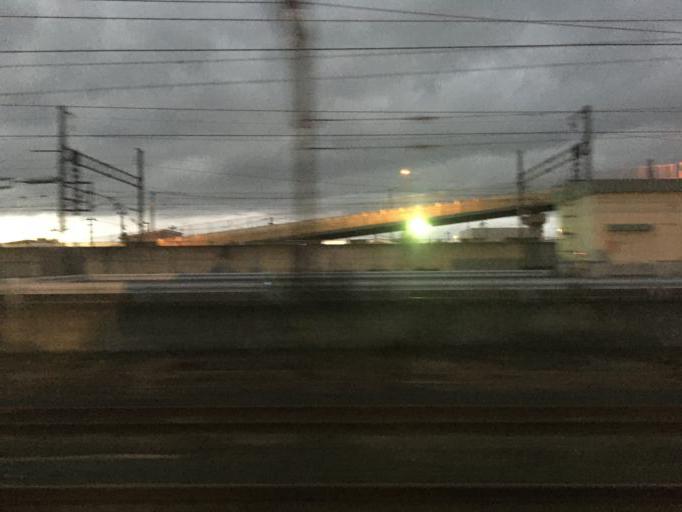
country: JP
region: Aomori
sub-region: Hachinohe Shi
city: Uchimaru
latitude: 40.5126
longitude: 141.4347
